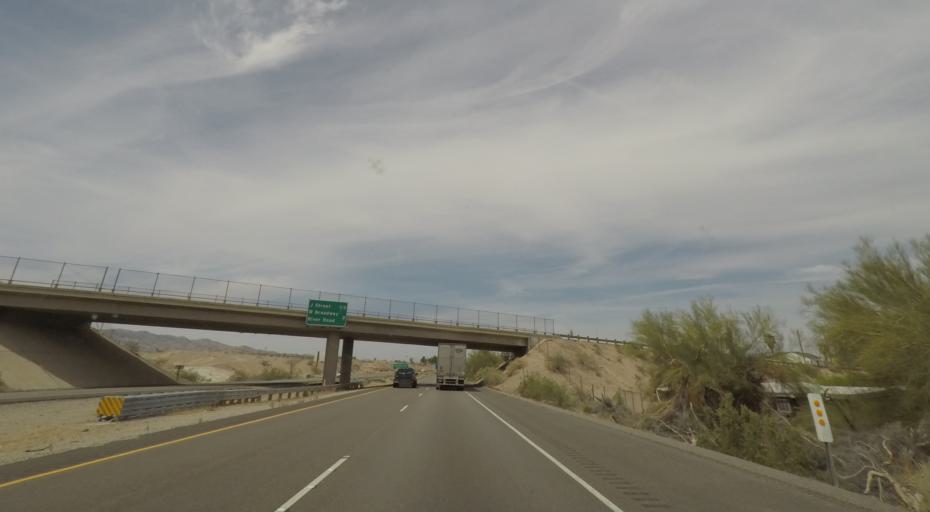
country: US
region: California
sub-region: San Bernardino County
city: Needles
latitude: 34.8328
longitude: -114.6045
